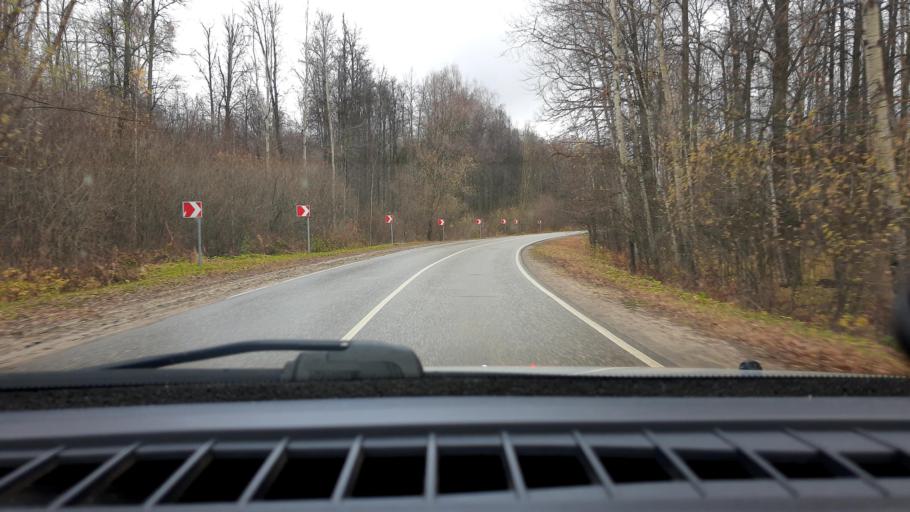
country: RU
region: Nizjnij Novgorod
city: Afonino
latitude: 56.1872
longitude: 44.0236
